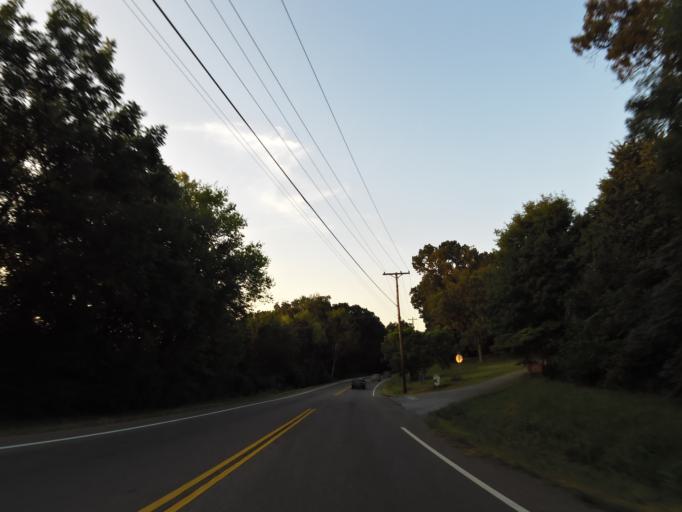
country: US
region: Tennessee
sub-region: Loudon County
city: Loudon
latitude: 35.7637
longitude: -84.3204
